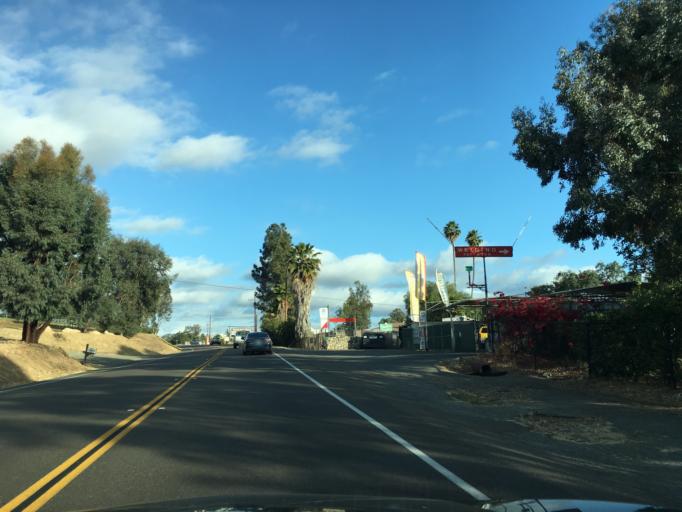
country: US
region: California
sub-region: San Diego County
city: Valley Center
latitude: 33.2383
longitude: -117.0536
